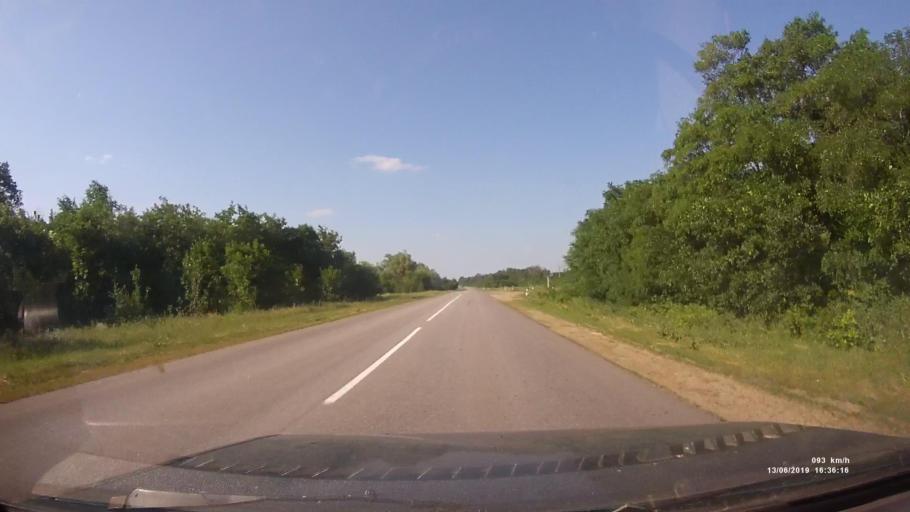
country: RU
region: Rostov
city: Kazanskaya
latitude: 49.8929
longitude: 41.3047
